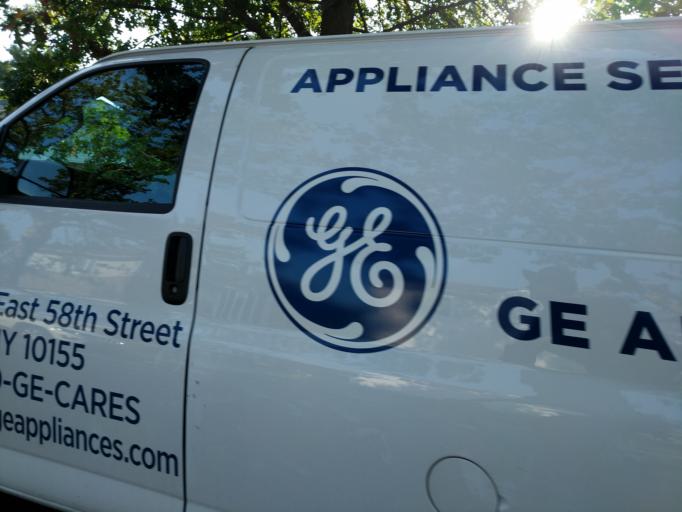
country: US
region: New York
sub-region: Nassau County
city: South Valley Stream
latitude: 40.6506
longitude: -73.7205
